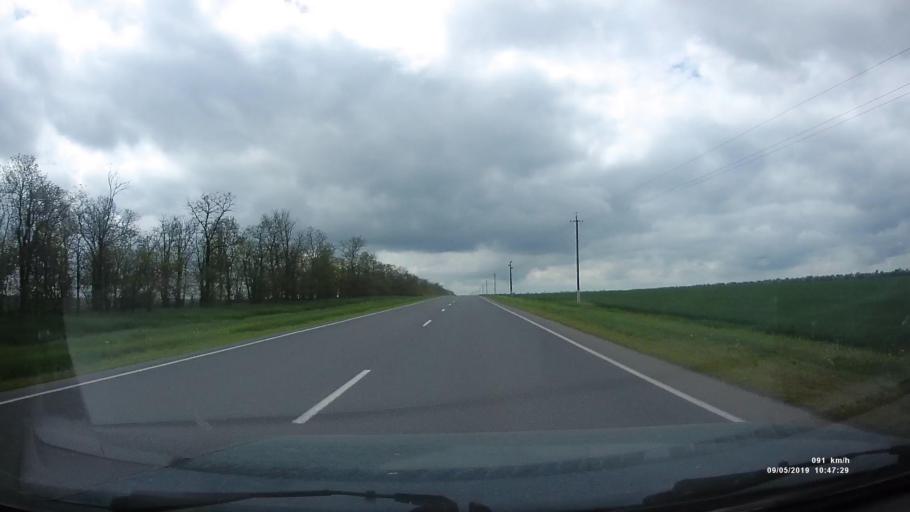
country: RU
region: Rostov
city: Peshkovo
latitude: 46.9701
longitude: 39.3556
